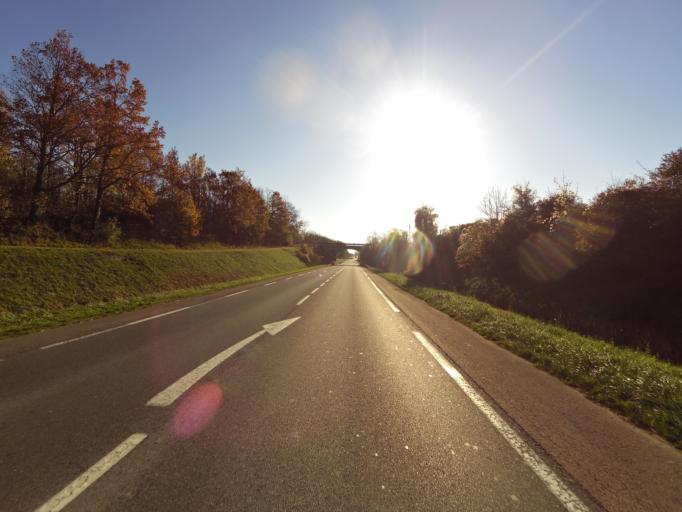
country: FR
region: Champagne-Ardenne
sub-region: Departement de l'Aube
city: Breviandes
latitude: 48.2543
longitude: 4.1057
